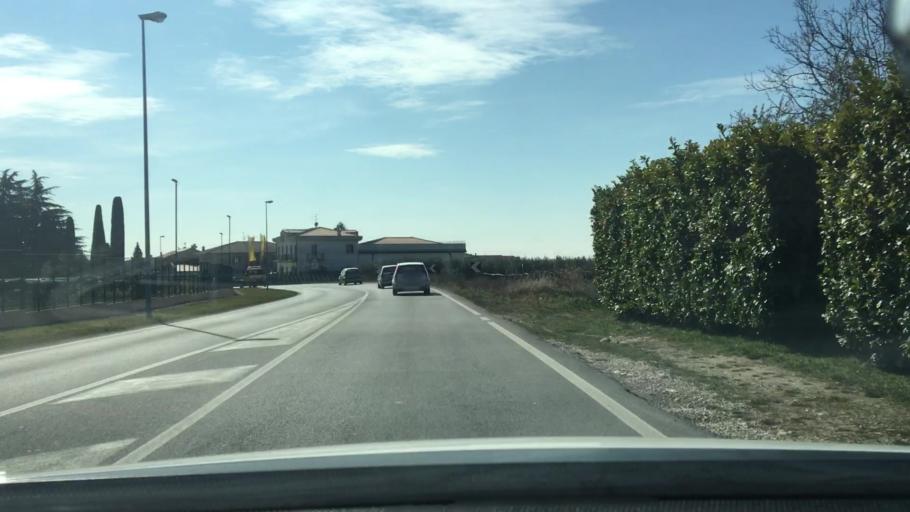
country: IT
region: Veneto
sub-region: Provincia di Verona
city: Cellore
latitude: 45.4914
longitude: 11.1752
